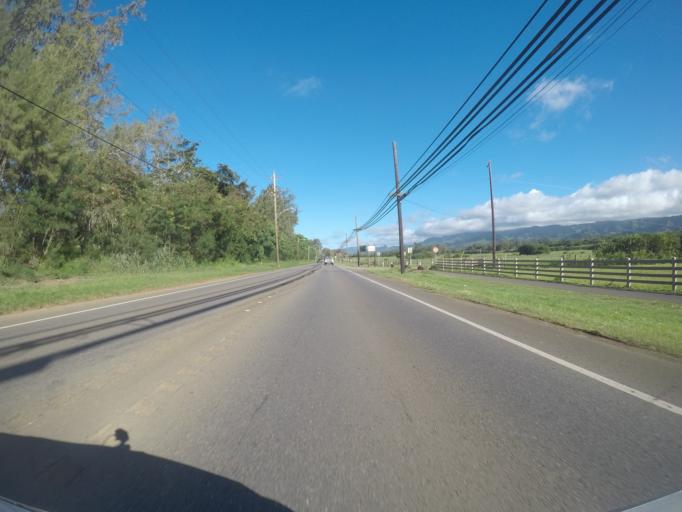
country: US
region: Hawaii
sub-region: Honolulu County
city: La'ie
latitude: 21.6622
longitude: -157.9348
